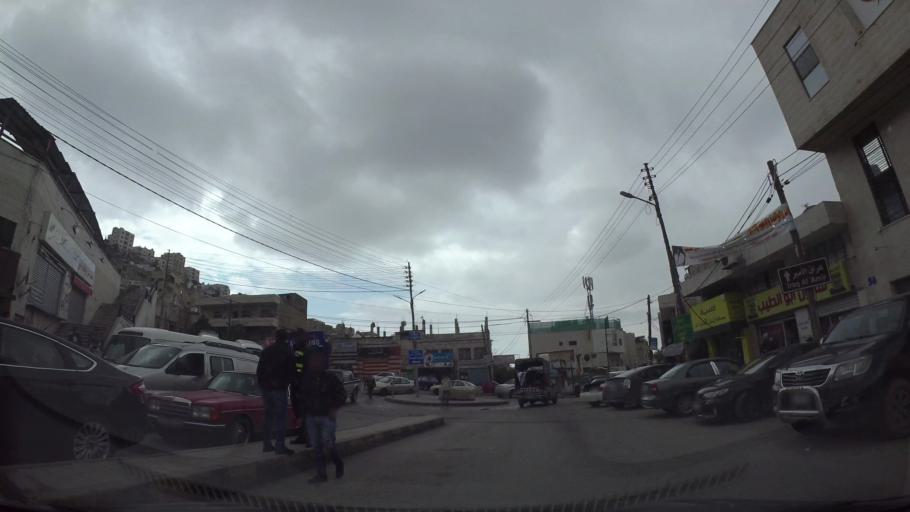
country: JO
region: Amman
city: Wadi as Sir
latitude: 31.9474
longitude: 35.8174
